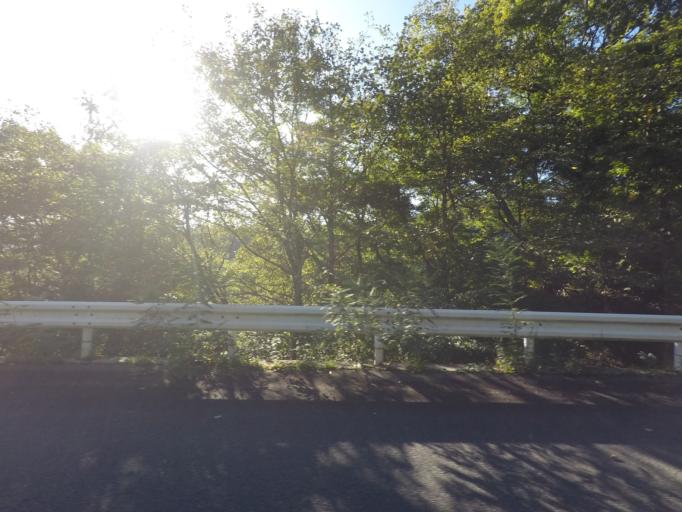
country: JP
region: Nagano
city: Tatsuno
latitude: 35.9752
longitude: 137.7726
